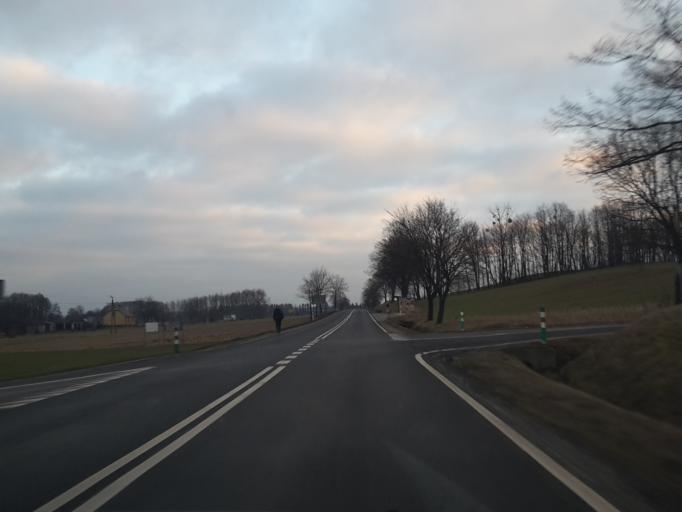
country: PL
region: Warmian-Masurian Voivodeship
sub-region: Powiat ilawski
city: Lubawa
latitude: 53.5642
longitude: 19.7789
